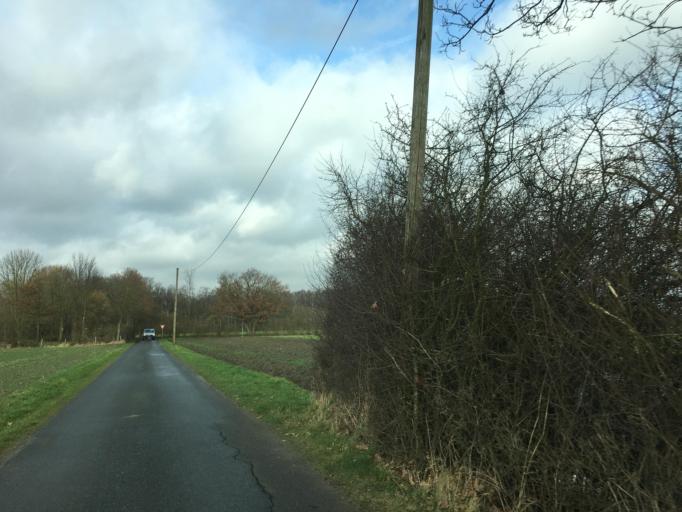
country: DE
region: North Rhine-Westphalia
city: Ludinghausen
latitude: 51.7863
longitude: 7.4732
